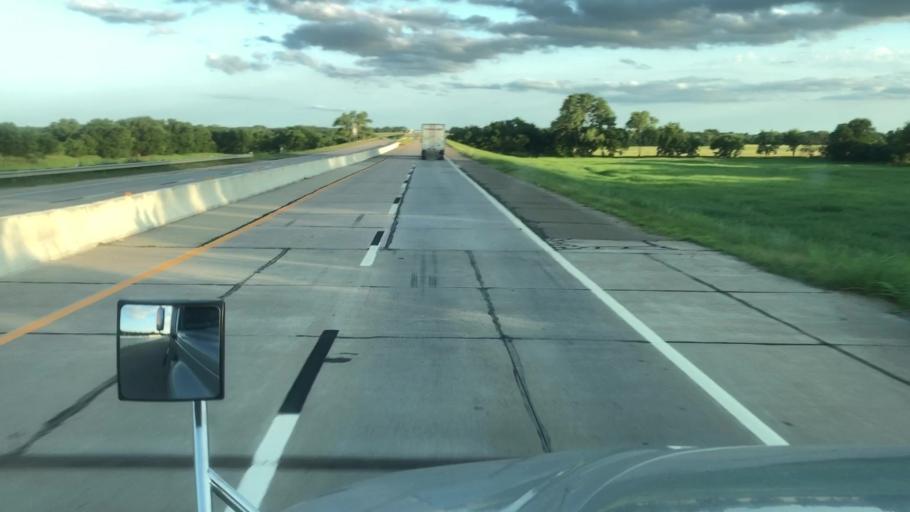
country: US
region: Oklahoma
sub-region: Pawnee County
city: Pawnee
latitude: 36.3074
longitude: -96.9906
